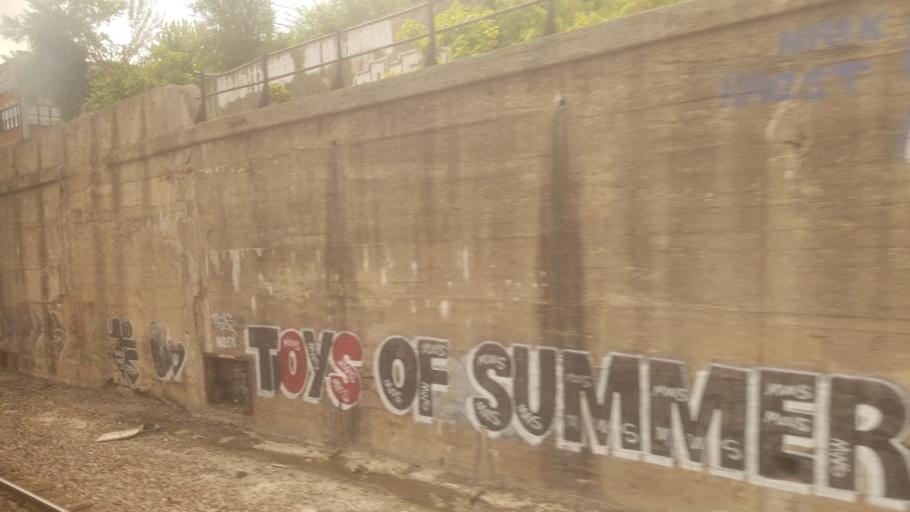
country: US
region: Missouri
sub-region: Jackson County
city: Kansas City
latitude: 39.0885
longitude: -94.5681
